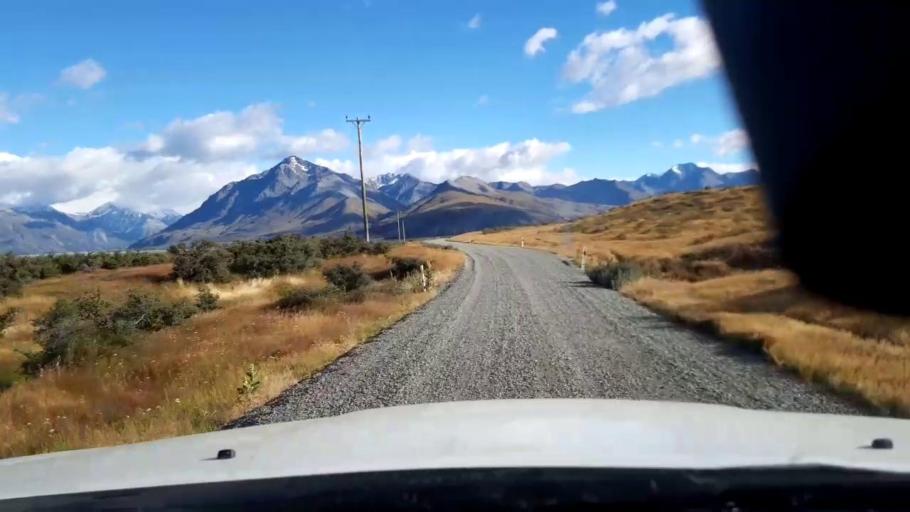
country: NZ
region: Canterbury
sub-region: Timaru District
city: Pleasant Point
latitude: -43.7593
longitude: 170.5698
